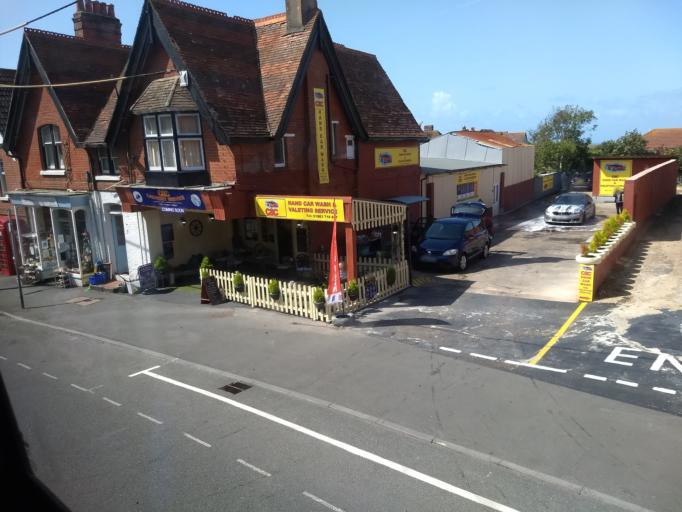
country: GB
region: England
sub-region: Isle of Wight
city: Totland
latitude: 50.6831
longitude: -1.5388
